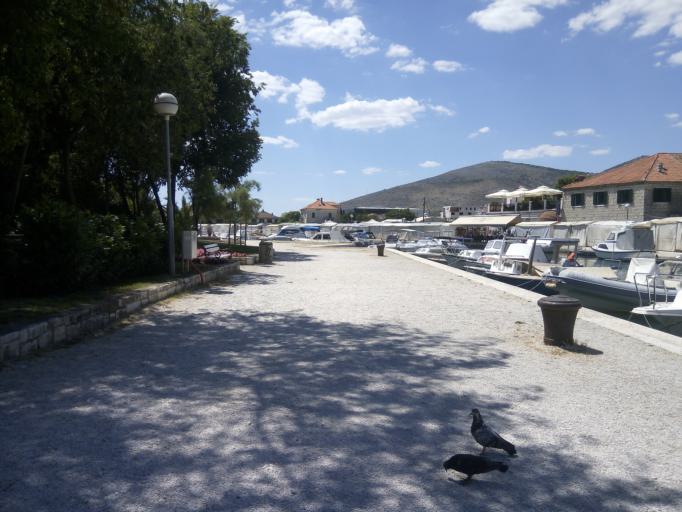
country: HR
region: Splitsko-Dalmatinska
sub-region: Grad Trogir
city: Trogir
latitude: 43.5179
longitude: 16.2501
